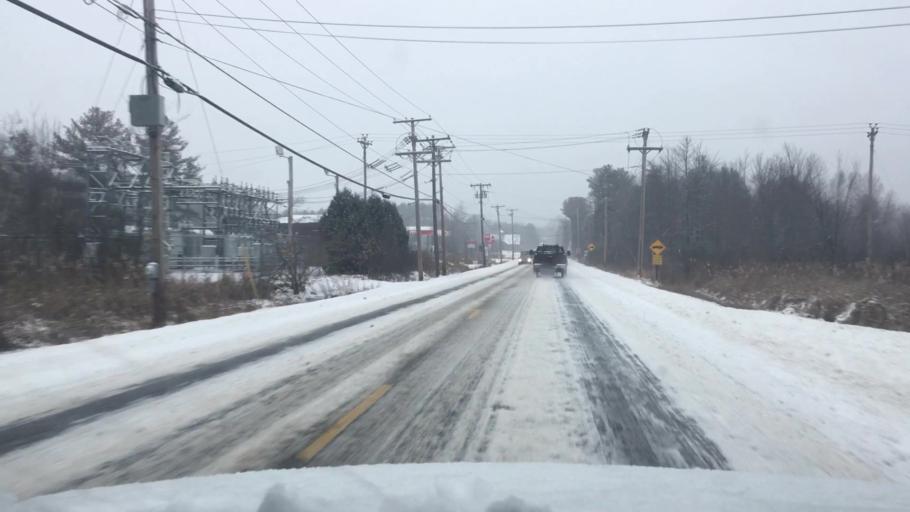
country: US
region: Maine
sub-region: Cumberland County
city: New Gloucester
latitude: 43.8770
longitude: -70.3280
